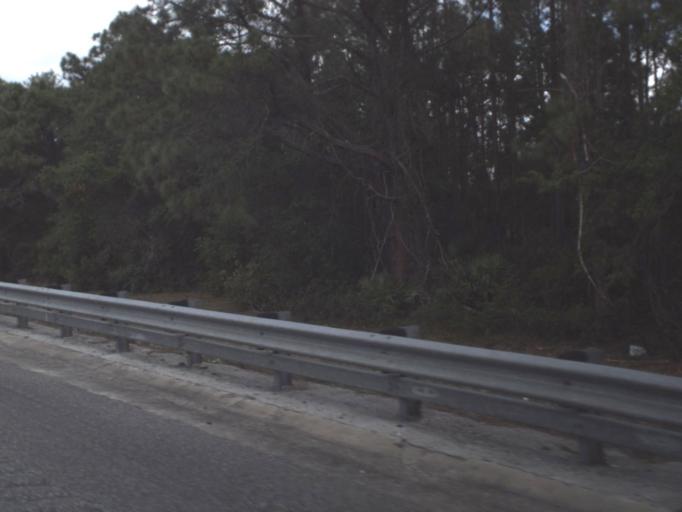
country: US
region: Florida
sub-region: Orange County
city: Wedgefield
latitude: 28.4525
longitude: -81.0240
